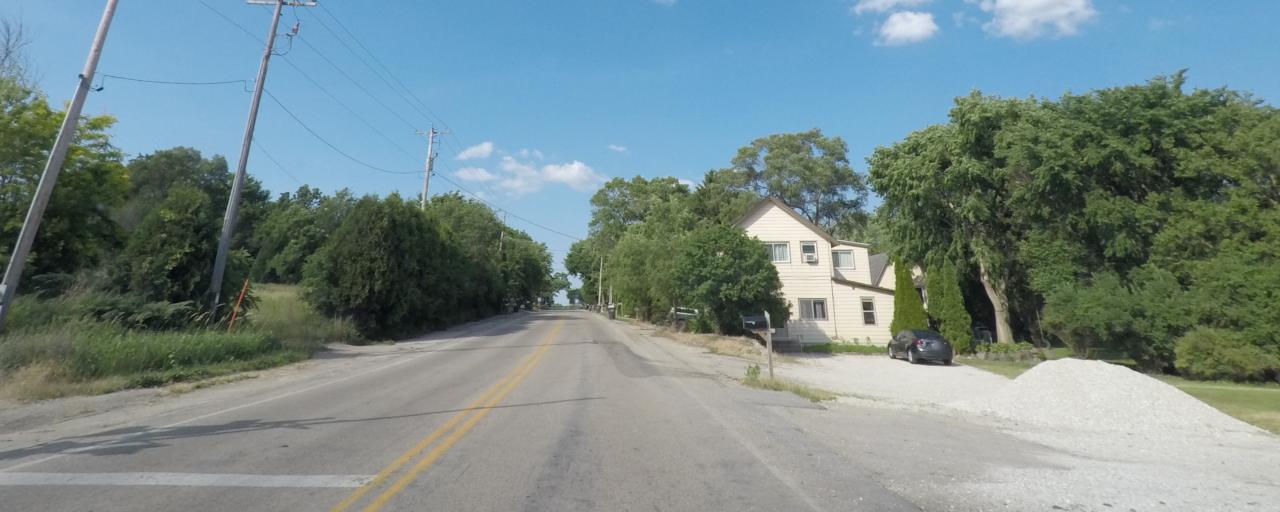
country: US
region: Wisconsin
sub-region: Walworth County
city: Potter Lake
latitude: 42.8217
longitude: -88.3217
